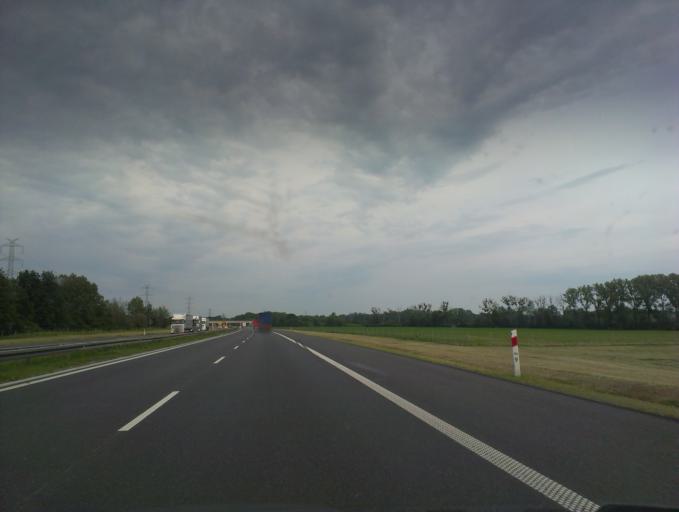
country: PL
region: Opole Voivodeship
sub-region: Powiat brzeski
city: Grodkow
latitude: 50.7701
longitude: 17.3844
